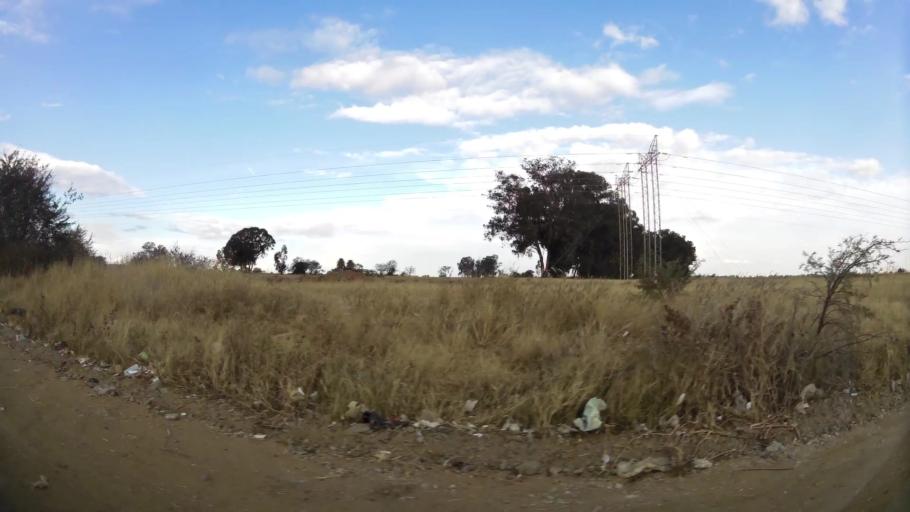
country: ZA
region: Orange Free State
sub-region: Lejweleputswa District Municipality
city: Welkom
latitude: -28.0093
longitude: 26.7283
